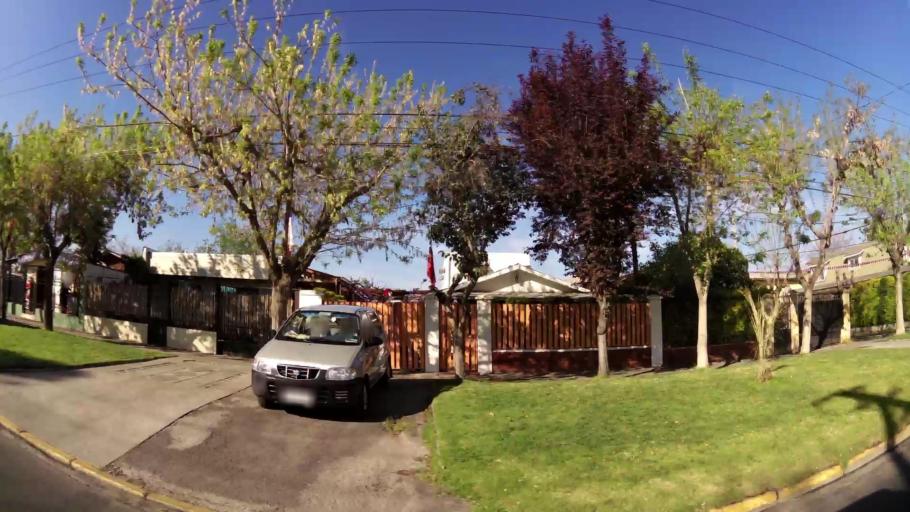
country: CL
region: Santiago Metropolitan
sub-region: Provincia de Santiago
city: Villa Presidente Frei, Nunoa, Santiago, Chile
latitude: -33.4621
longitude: -70.5638
